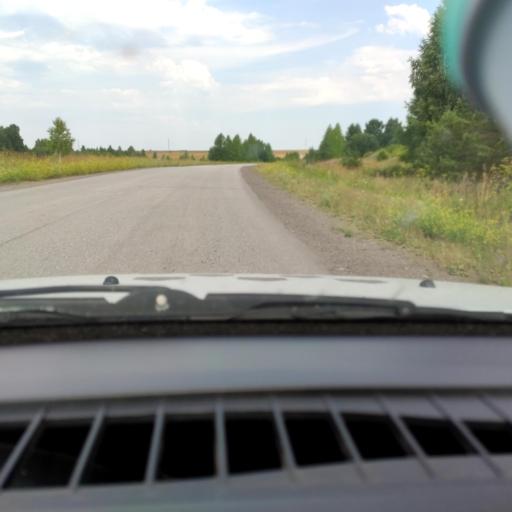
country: RU
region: Perm
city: Orda
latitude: 57.1877
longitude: 56.8502
